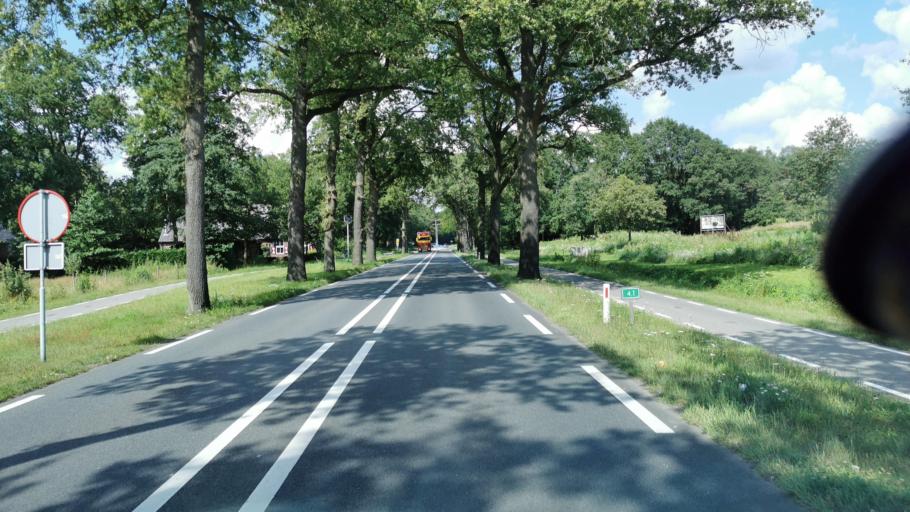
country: NL
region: Overijssel
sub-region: Gemeente Oldenzaal
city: Oldenzaal
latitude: 52.2661
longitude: 6.9242
